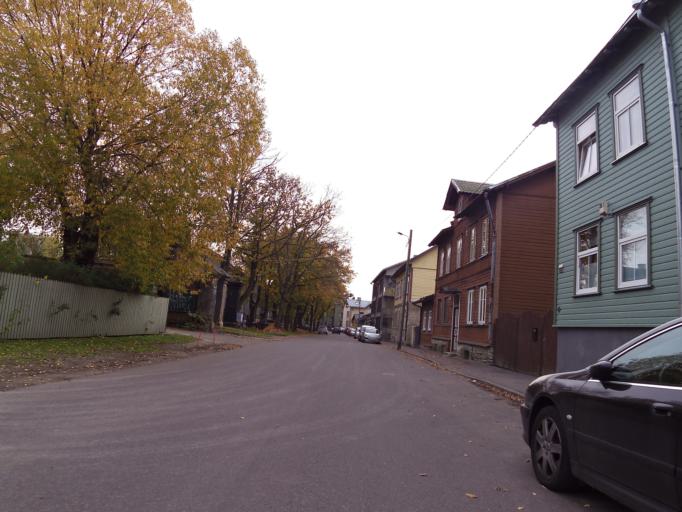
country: EE
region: Harju
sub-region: Tallinna linn
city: Tallinn
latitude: 59.4412
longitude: 24.7190
